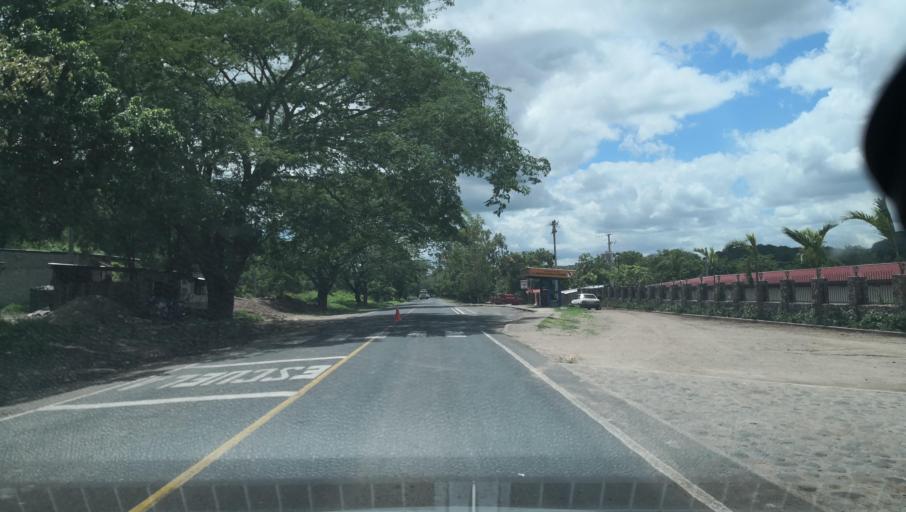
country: NI
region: Madriz
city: Palacaguina
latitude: 13.4220
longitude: -86.4016
